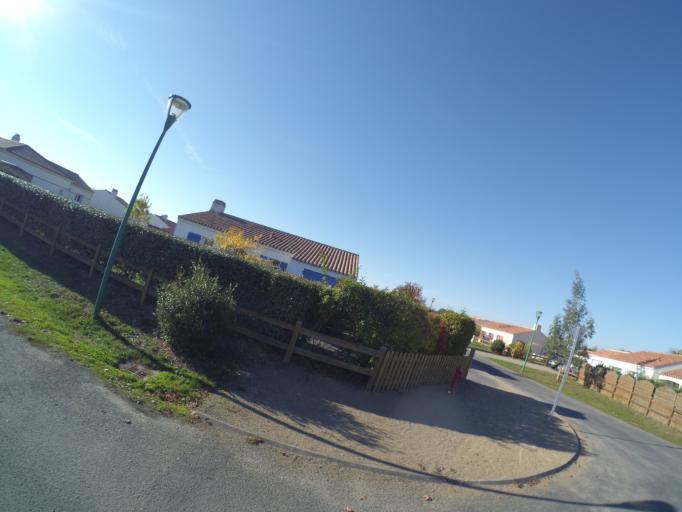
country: FR
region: Pays de la Loire
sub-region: Departement de la Loire-Atlantique
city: Saint-Lumine-de-Clisson
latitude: 47.0846
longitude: -1.3380
